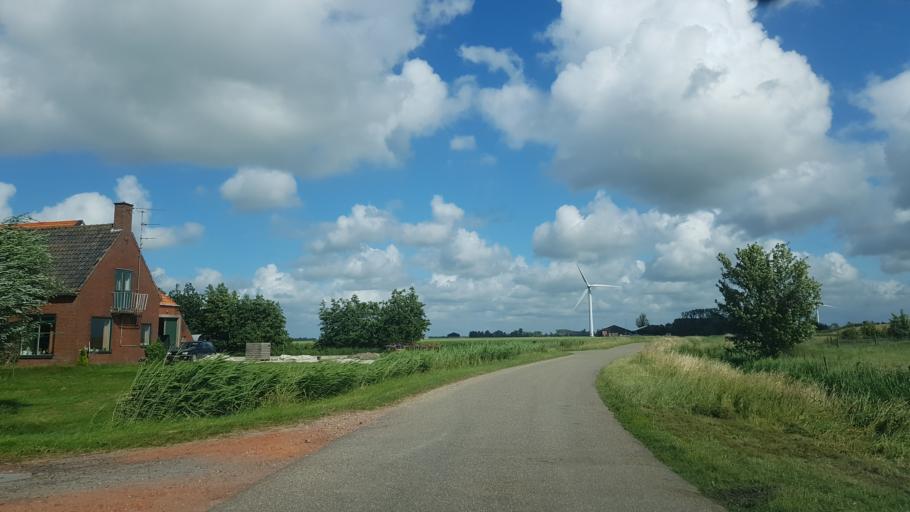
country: NL
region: Groningen
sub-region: Gemeente Winsum
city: Winsum
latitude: 53.4156
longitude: 6.4889
